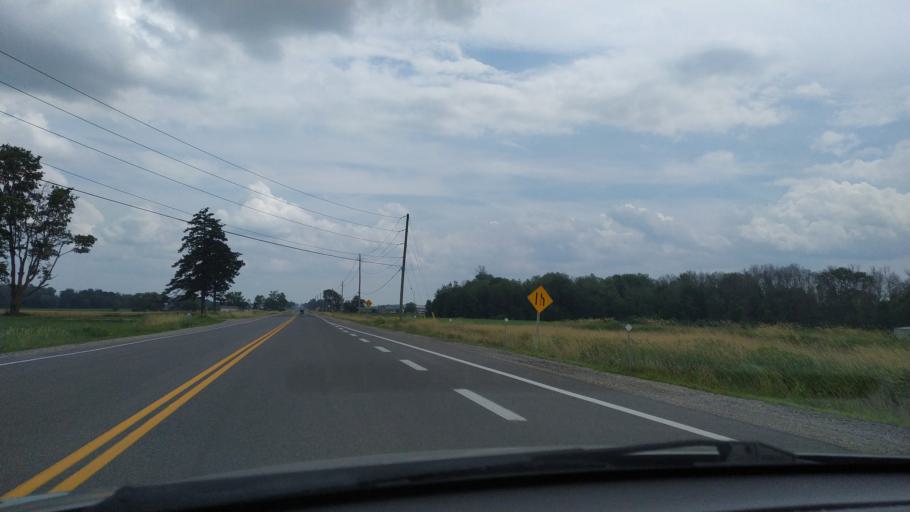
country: CA
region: Ontario
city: Stratford
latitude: 43.3703
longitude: -80.9087
